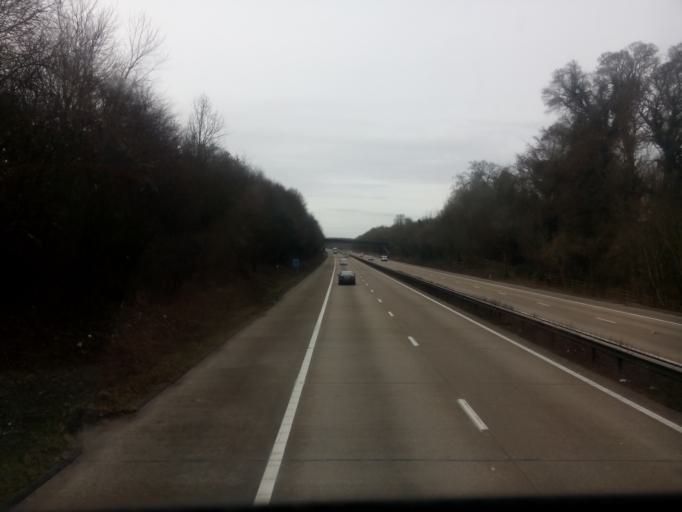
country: GB
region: England
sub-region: Hampshire
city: Overton
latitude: 51.1586
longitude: -1.2353
